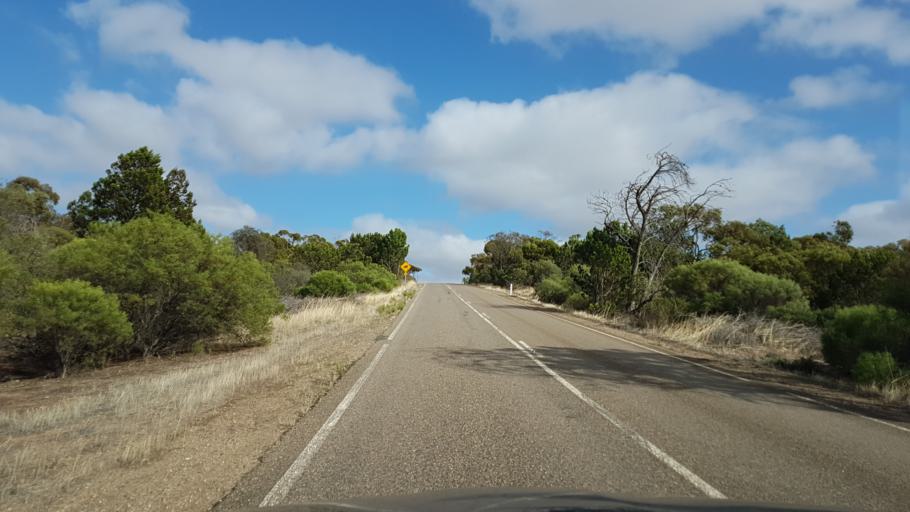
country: AU
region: South Australia
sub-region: Murray Bridge
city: Murray Bridge
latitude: -35.1140
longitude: 139.2280
